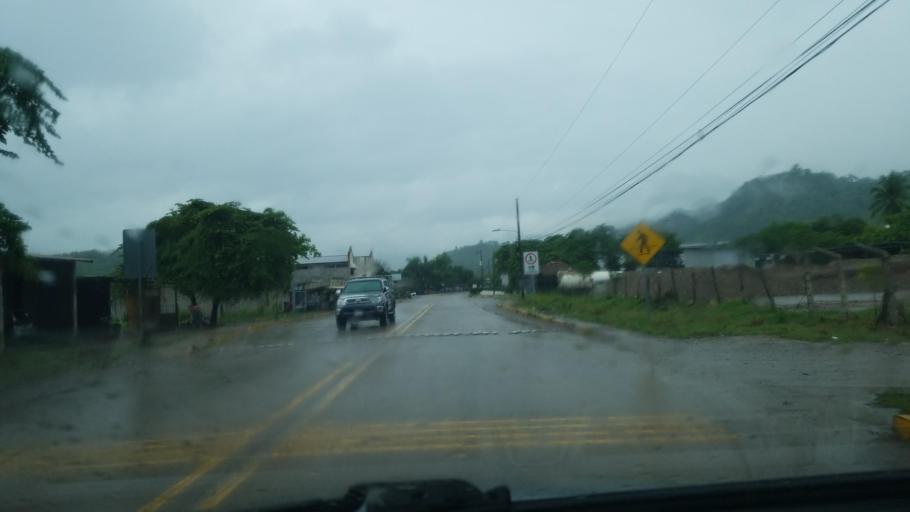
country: HN
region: Copan
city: Copan
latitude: 14.8346
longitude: -89.1567
